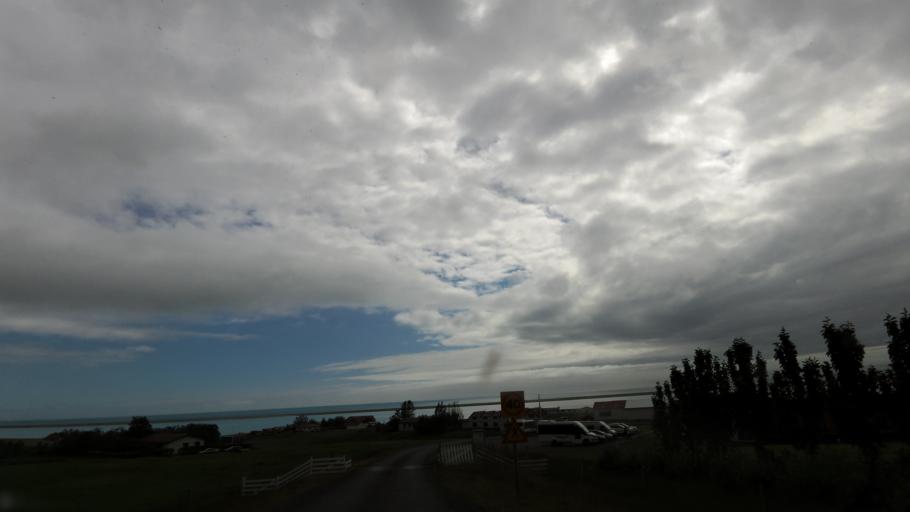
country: IS
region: East
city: Hoefn
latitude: 64.1304
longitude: -16.0182
